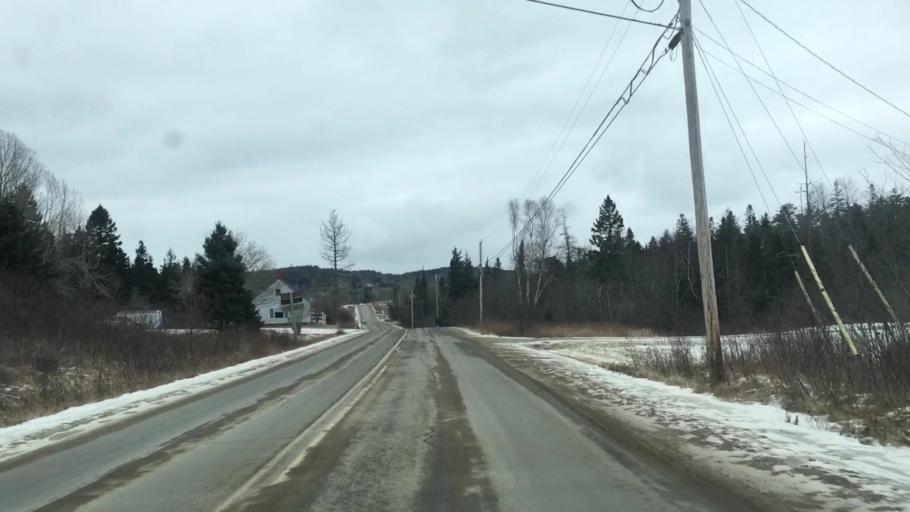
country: US
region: Maine
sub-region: Washington County
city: Machiasport
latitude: 44.7067
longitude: -67.4027
